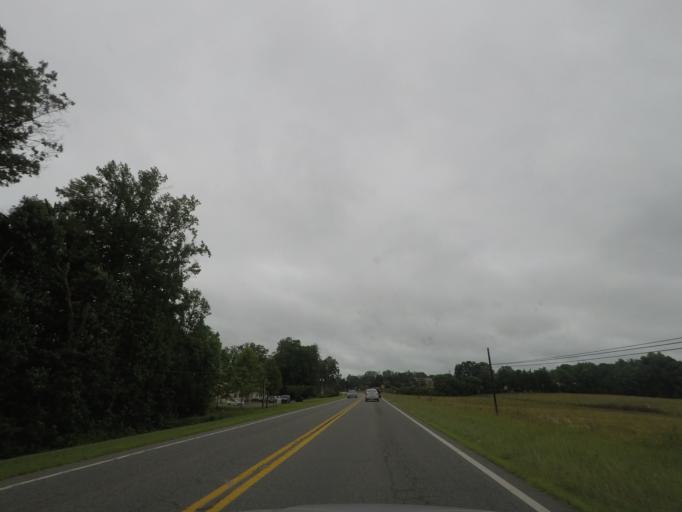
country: US
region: Virginia
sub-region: Fluvanna County
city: Palmyra
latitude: 37.8084
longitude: -78.2397
